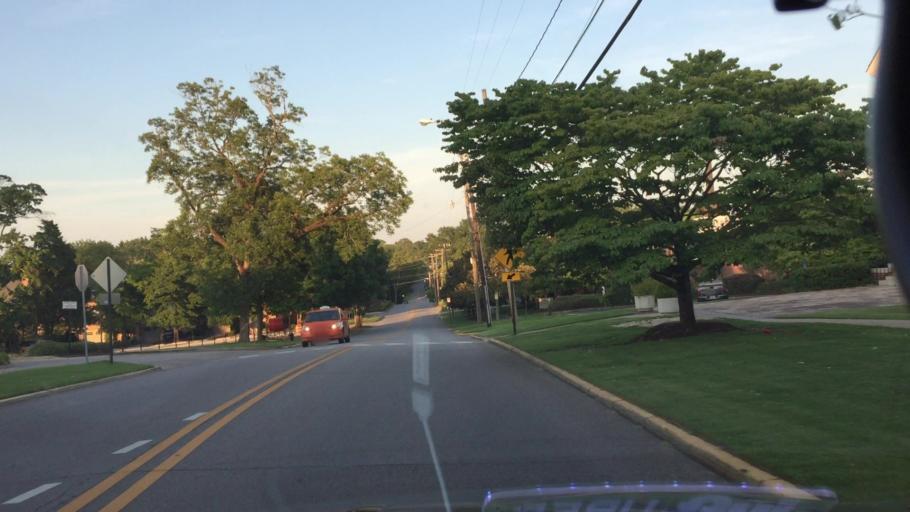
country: US
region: Alabama
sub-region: Lee County
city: Auburn
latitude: 32.6065
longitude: -85.4793
